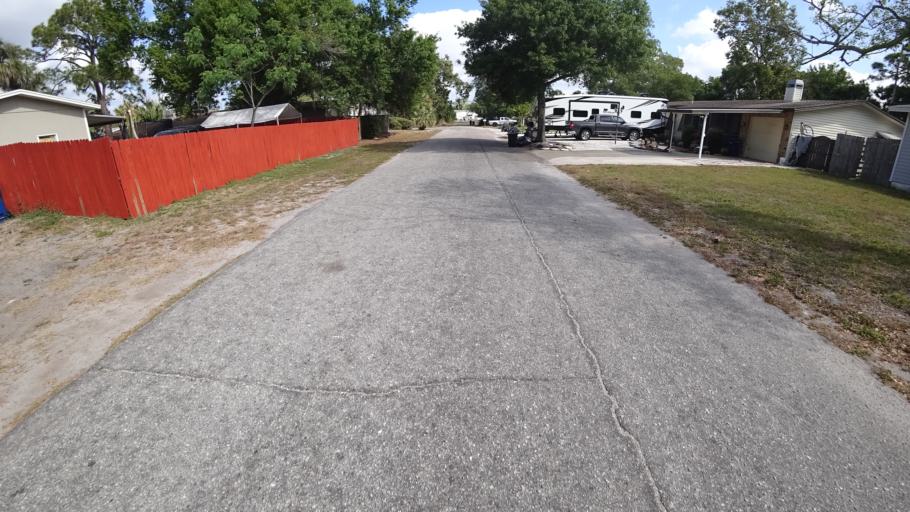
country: US
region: Florida
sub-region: Manatee County
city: Whitfield
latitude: 27.4246
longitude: -82.5636
